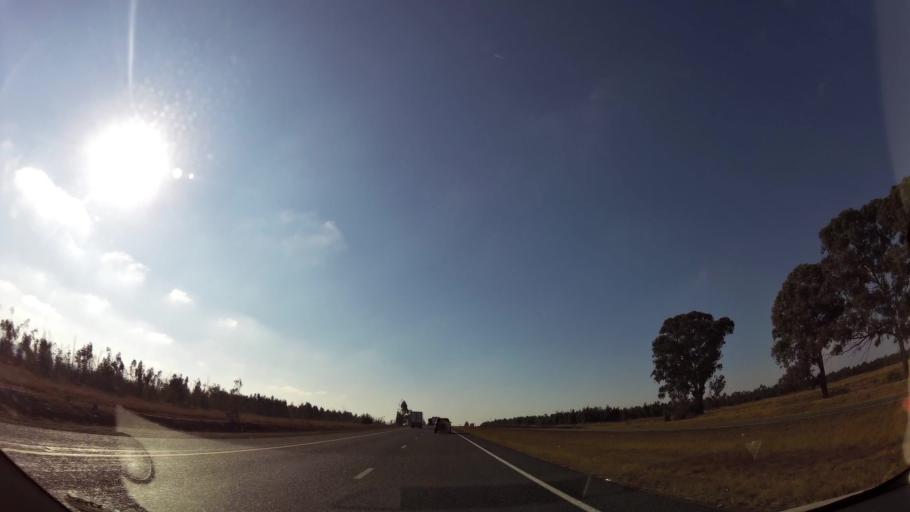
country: ZA
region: Mpumalanga
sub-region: Nkangala District Municipality
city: Delmas
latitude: -26.0188
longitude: 28.9129
